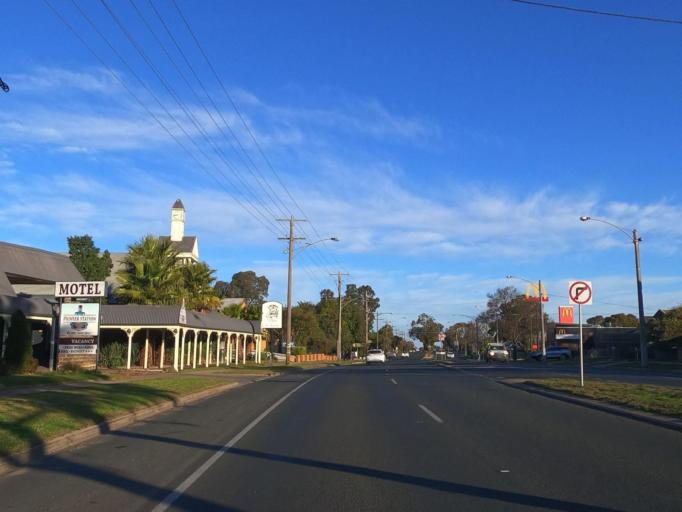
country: AU
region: Victoria
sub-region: Swan Hill
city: Swan Hill
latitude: -35.3472
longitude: 143.5618
